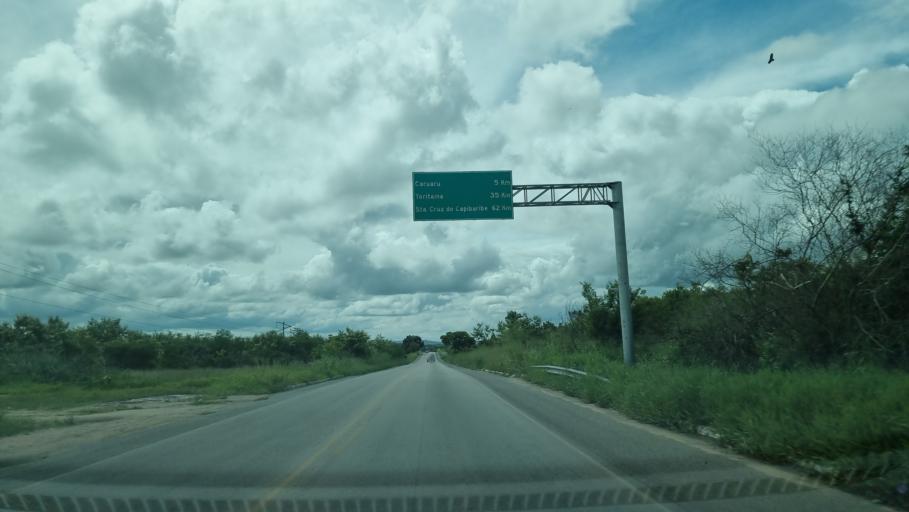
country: BR
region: Pernambuco
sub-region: Caruaru
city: Caruaru
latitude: -8.3428
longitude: -35.9828
